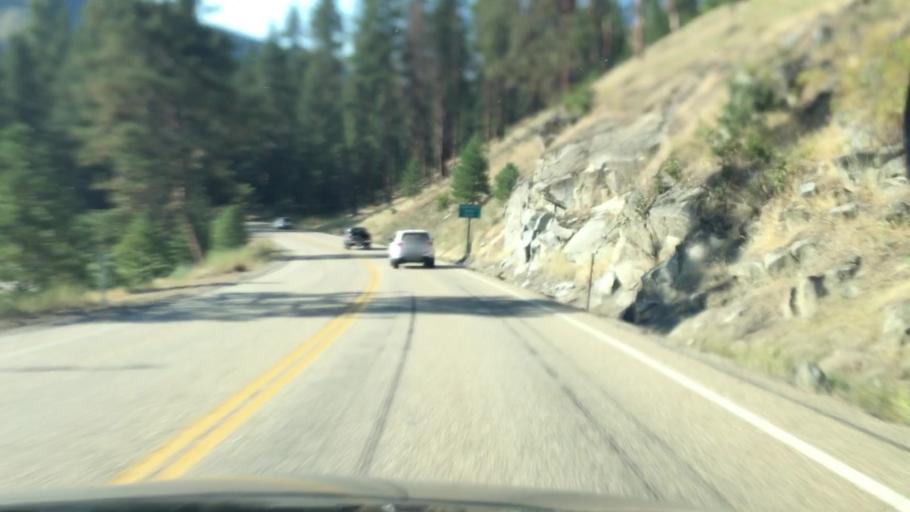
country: US
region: Idaho
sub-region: Boise County
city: Idaho City
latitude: 44.0722
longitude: -116.1185
